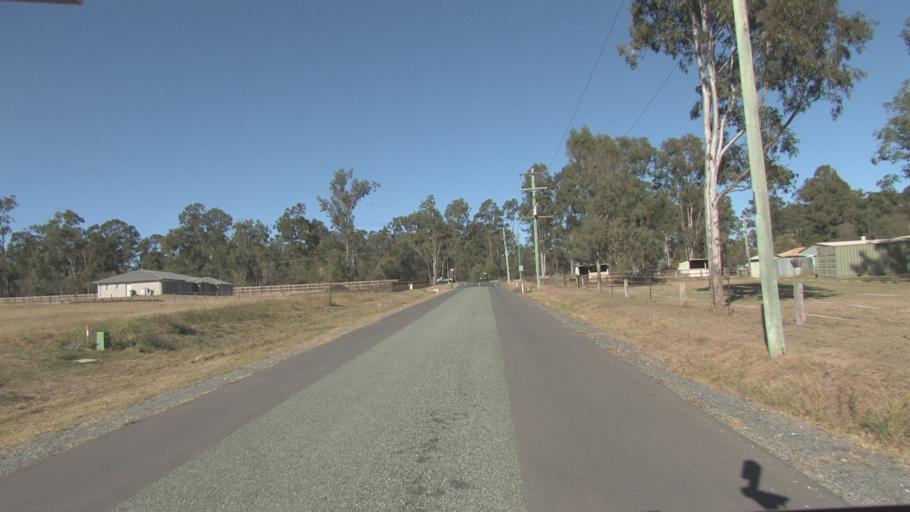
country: AU
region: Queensland
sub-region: Logan
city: North Maclean
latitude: -27.8136
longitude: 152.9923
